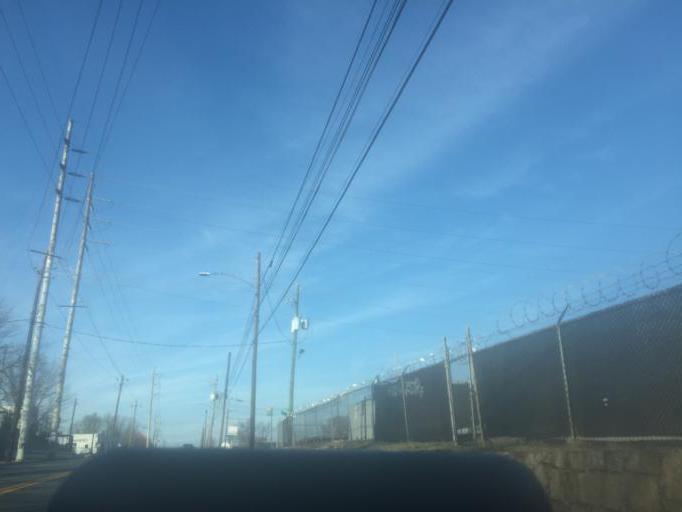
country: US
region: Georgia
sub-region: Fulton County
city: Atlanta
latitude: 33.7356
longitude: -84.4081
